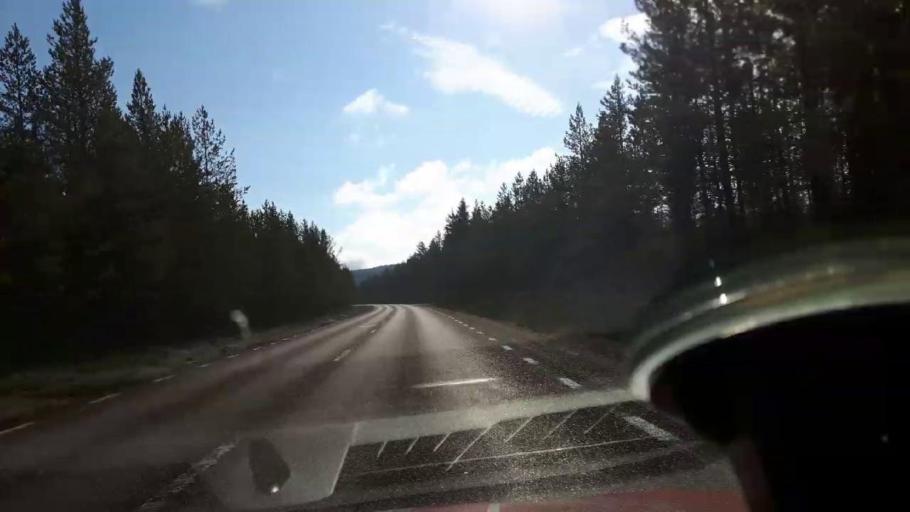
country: SE
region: Gaevleborg
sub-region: Ljusdals Kommun
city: Farila
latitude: 61.8967
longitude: 15.6536
